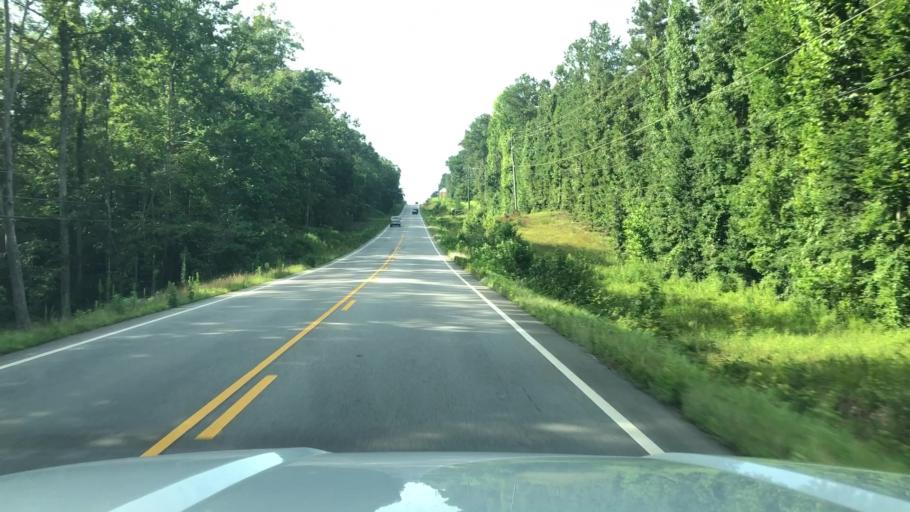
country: US
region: Georgia
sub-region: Paulding County
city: Dallas
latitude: 33.9444
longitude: -84.8467
